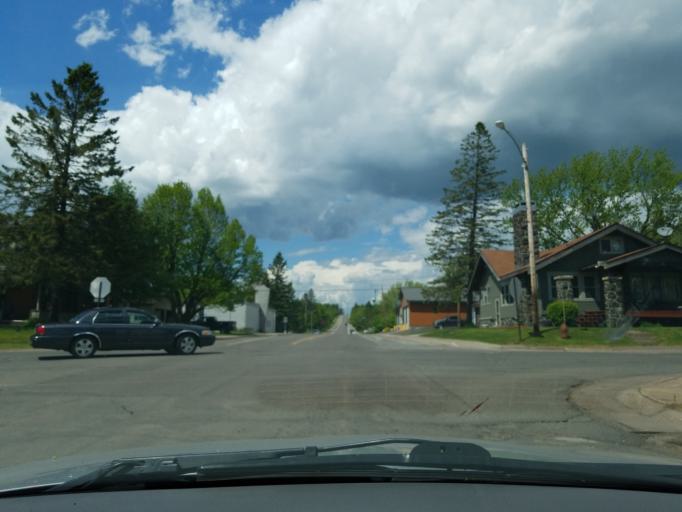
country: US
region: Minnesota
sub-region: Saint Louis County
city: Proctor
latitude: 46.7468
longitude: -92.2223
